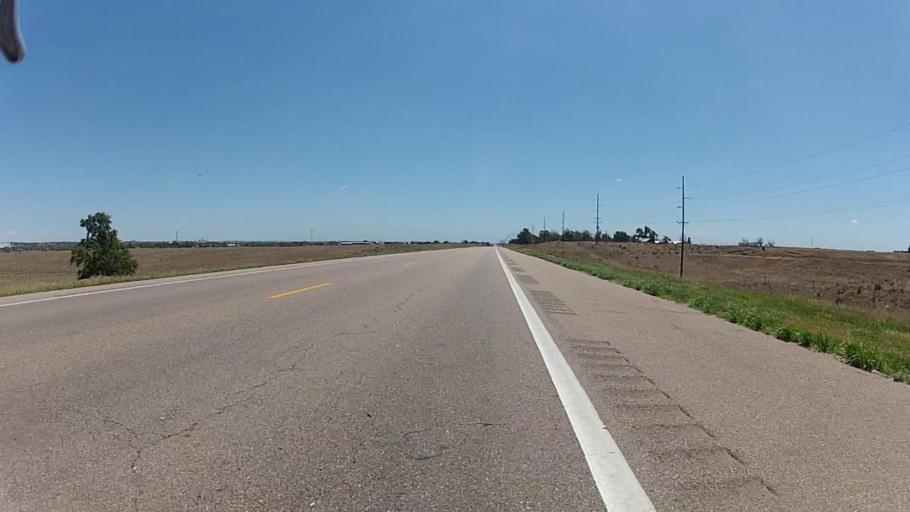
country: US
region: Kansas
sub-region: Ford County
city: Dodge City
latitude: 37.7224
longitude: -100.0450
